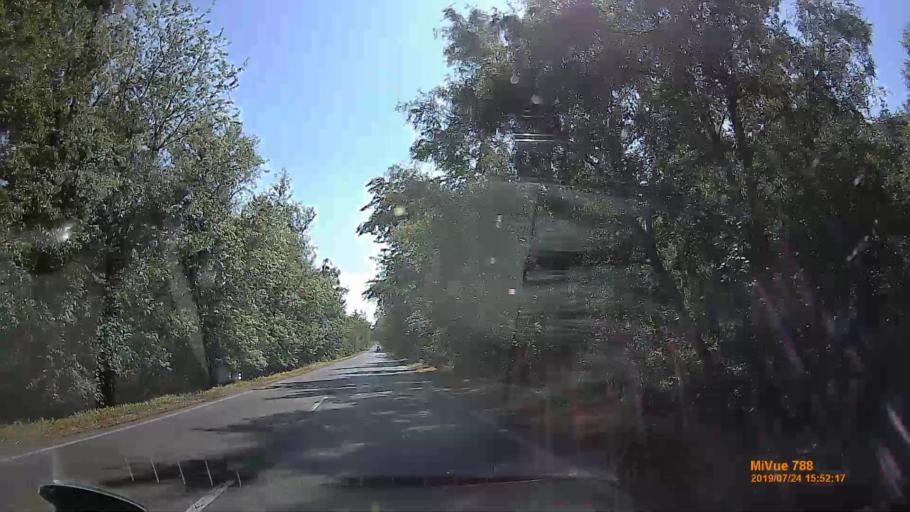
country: HU
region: Szabolcs-Szatmar-Bereg
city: Vaja
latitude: 48.0315
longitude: 22.1685
